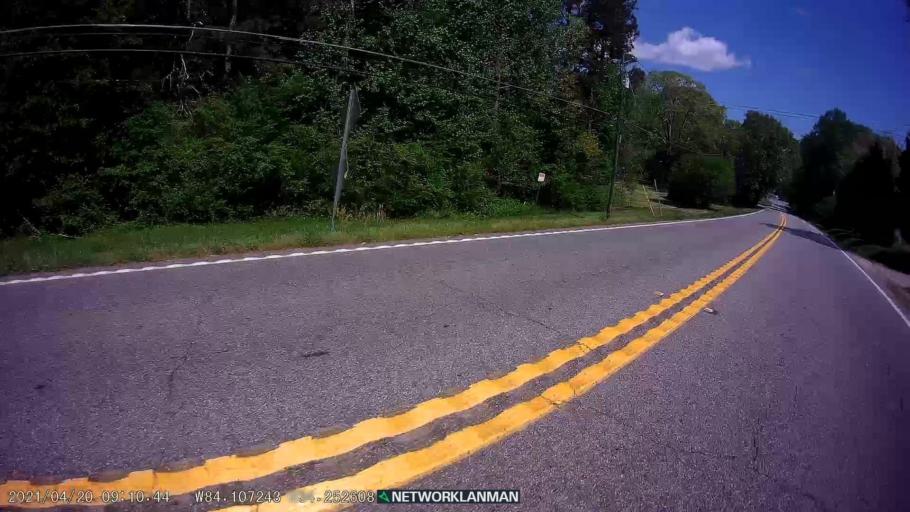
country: US
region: Georgia
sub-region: Forsyth County
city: Cumming
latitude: 34.2540
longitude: -84.1083
